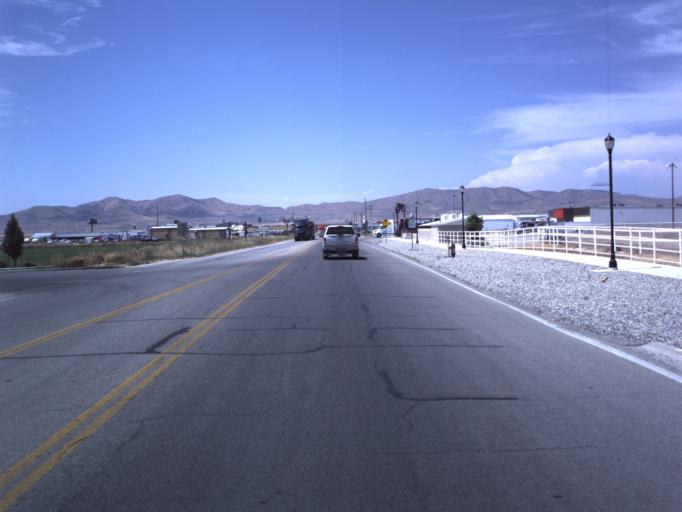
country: US
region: Utah
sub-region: Box Elder County
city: Tremonton
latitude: 41.7113
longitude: -112.1817
